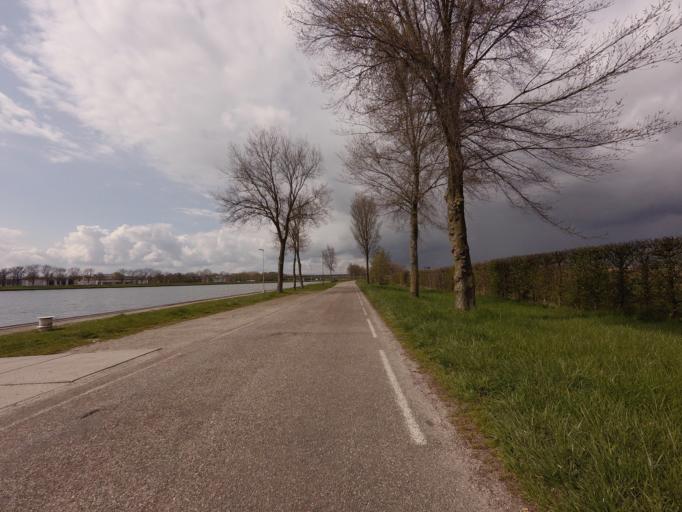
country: NL
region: Utrecht
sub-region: Gemeente Utrecht
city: Lunetten
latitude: 52.0387
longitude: 5.1143
